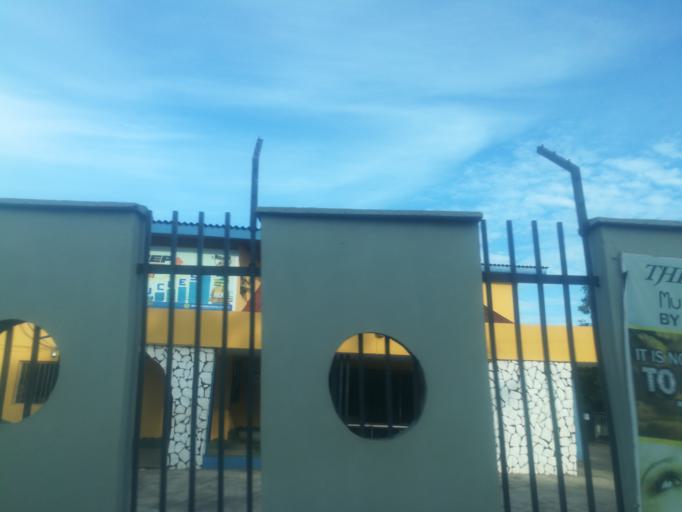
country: NG
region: Oyo
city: Ibadan
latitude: 7.3392
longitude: 3.8904
